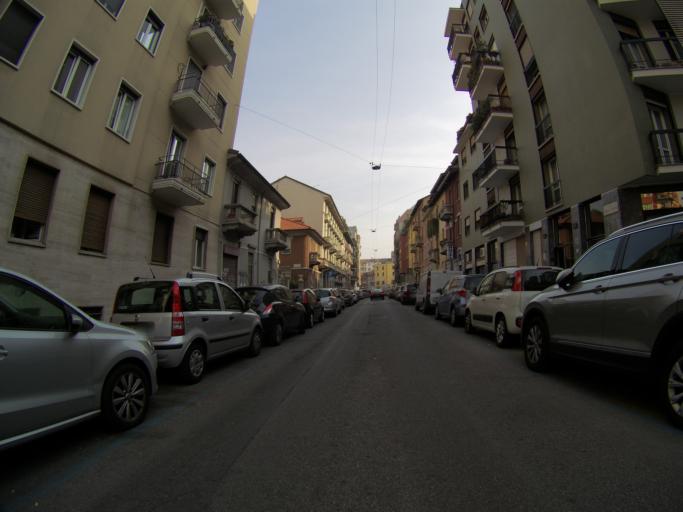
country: IT
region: Lombardy
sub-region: Citta metropolitana di Milano
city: Milano
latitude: 45.4667
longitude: 9.2267
